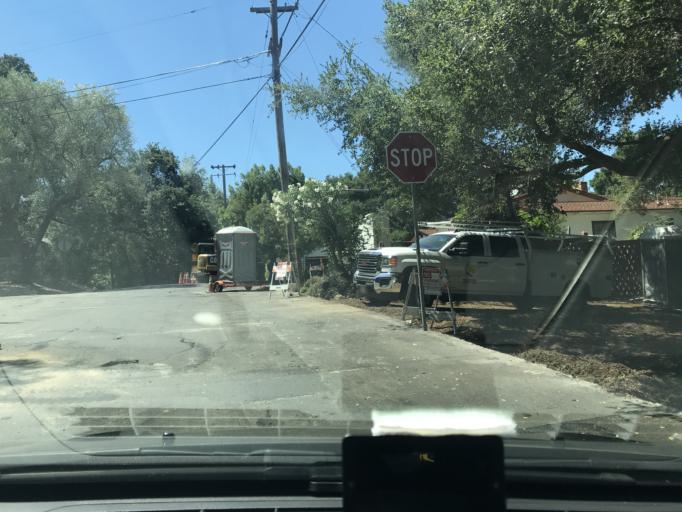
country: US
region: California
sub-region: Santa Clara County
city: Monte Sereno
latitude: 37.2285
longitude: -121.9925
